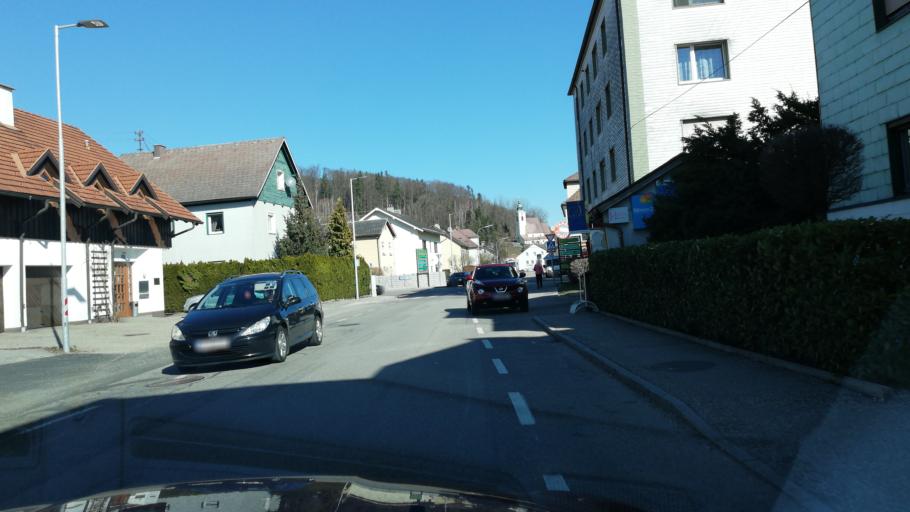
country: AT
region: Upper Austria
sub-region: Politischer Bezirk Vocklabruck
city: Attnang-Puchheim
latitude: 48.0167
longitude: 13.7198
